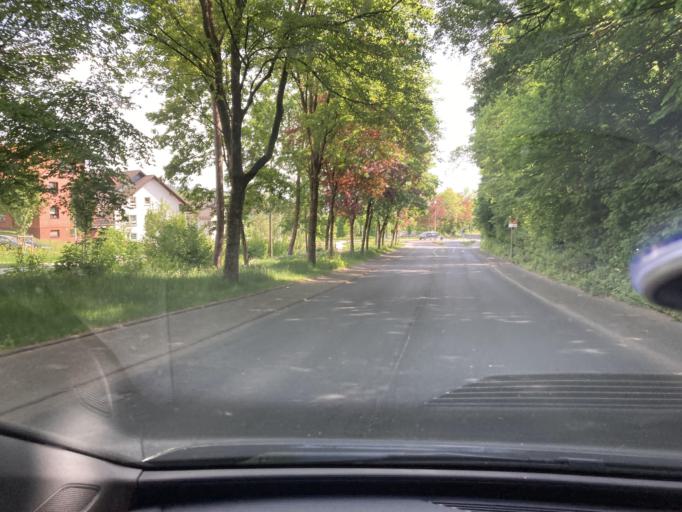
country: DE
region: North Rhine-Westphalia
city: Kreuztal
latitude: 50.9674
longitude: 7.9902
